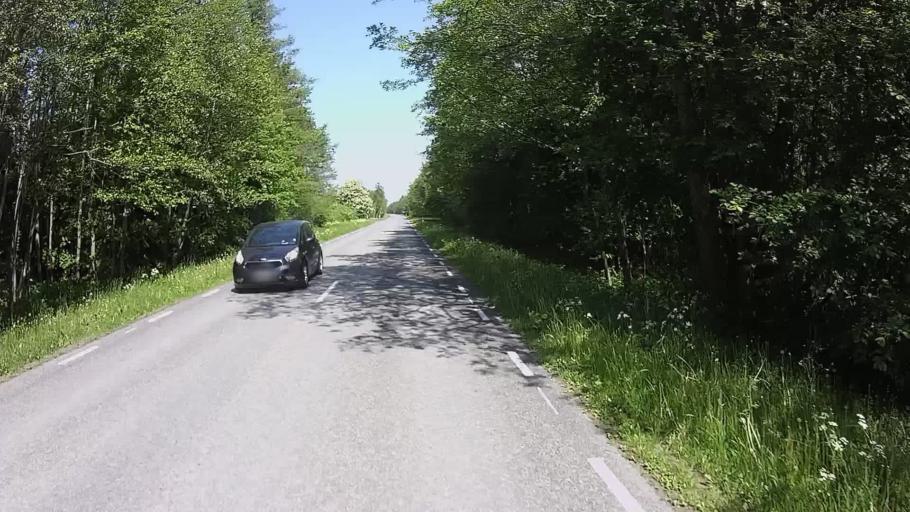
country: EE
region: Saare
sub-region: Kuressaare linn
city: Kuressaare
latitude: 58.1355
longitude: 22.2475
